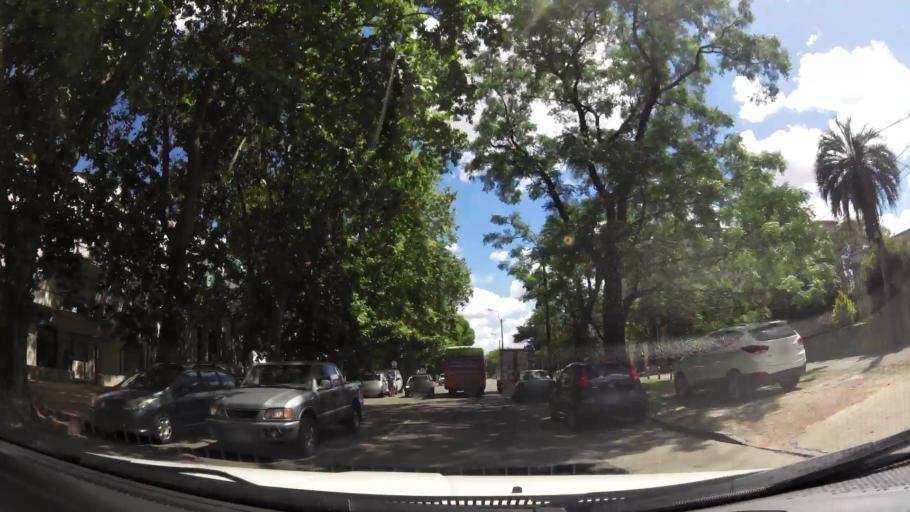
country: UY
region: Montevideo
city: Montevideo
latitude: -34.8734
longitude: -56.1965
